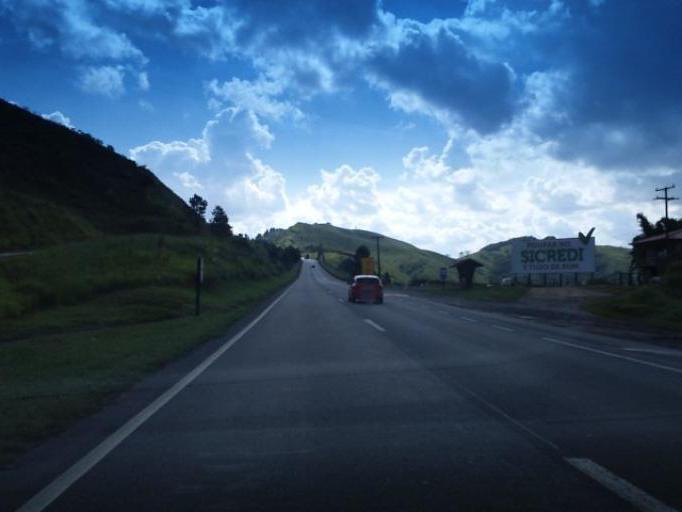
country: BR
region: Parana
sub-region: Campina Grande Do Sul
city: Campina Grande do Sul
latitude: -25.1007
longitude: -48.8270
